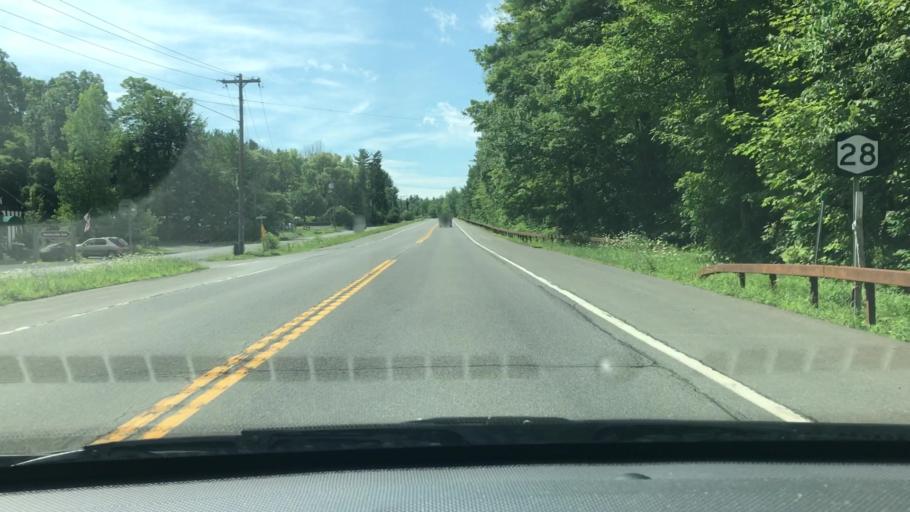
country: US
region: New York
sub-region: Ulster County
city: Shokan
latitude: 41.9989
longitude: -74.2646
